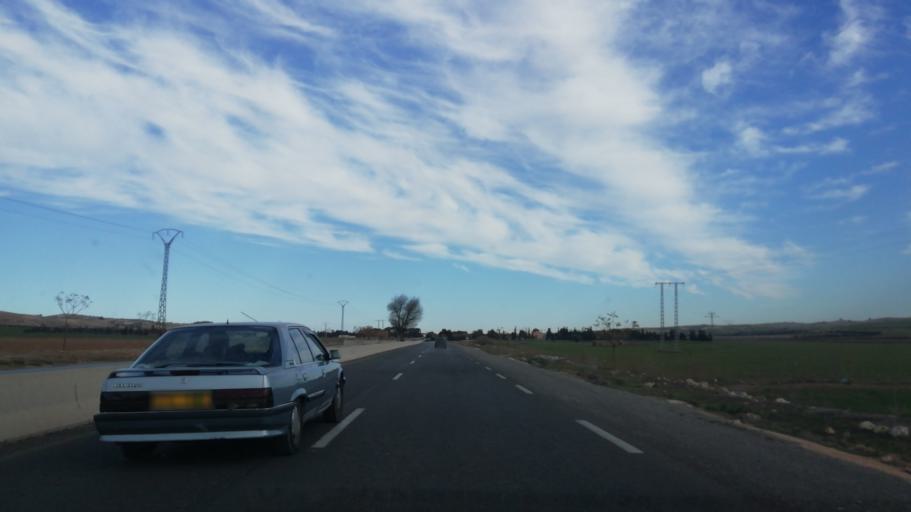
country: DZ
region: Sidi Bel Abbes
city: Sfizef
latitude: 35.1851
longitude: -0.3895
